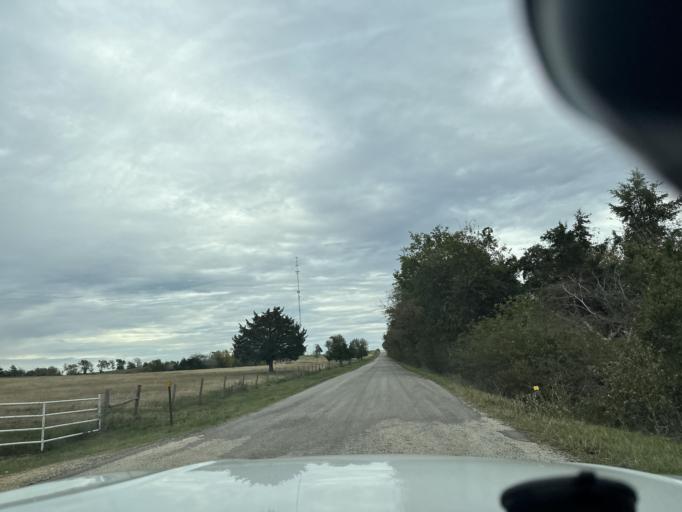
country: US
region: Texas
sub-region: Burleson County
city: Somerville
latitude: 30.1574
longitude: -96.6401
